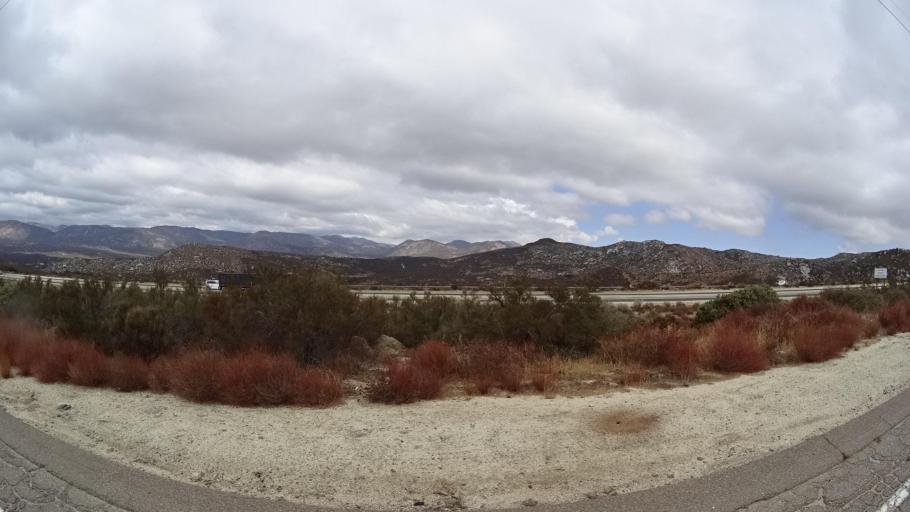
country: US
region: California
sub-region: San Diego County
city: Campo
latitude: 32.7191
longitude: -116.3928
